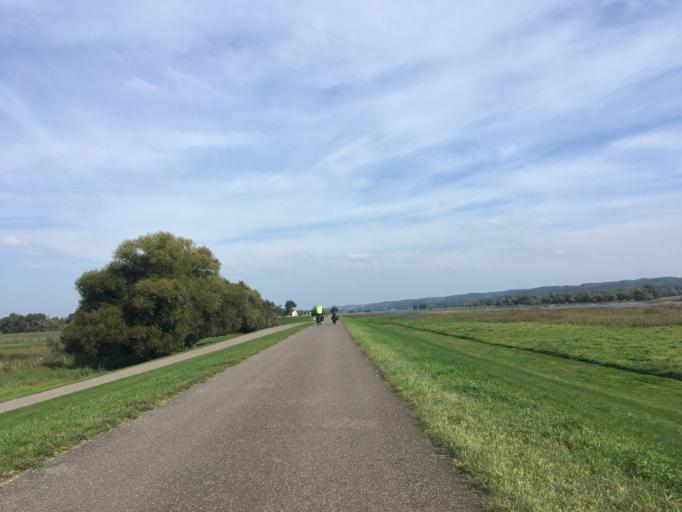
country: DE
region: Brandenburg
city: Schoneberg
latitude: 52.9809
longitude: 14.1849
